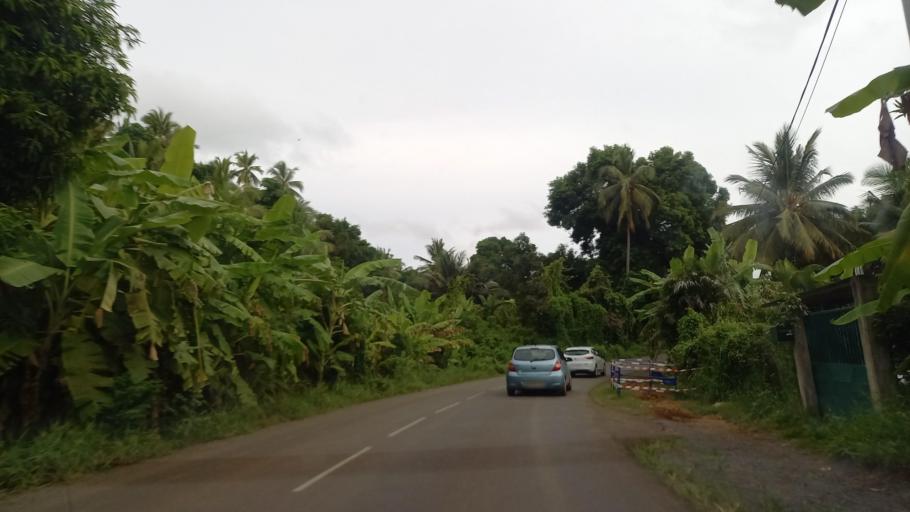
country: YT
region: Sada
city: Sada
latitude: -12.8581
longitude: 45.1034
